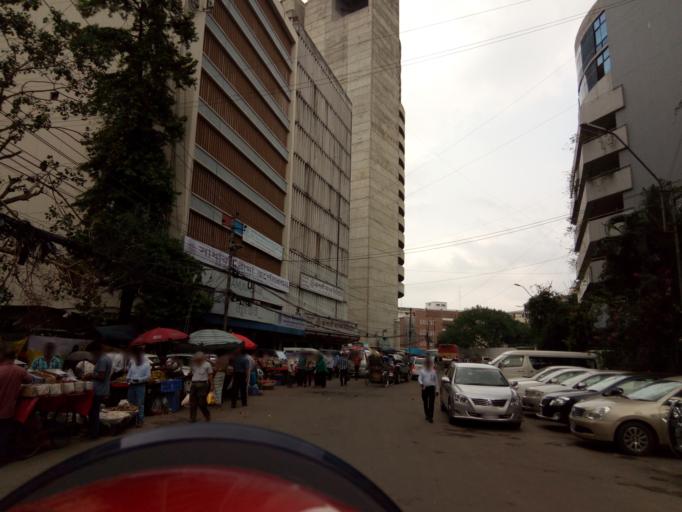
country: BD
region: Dhaka
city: Paltan
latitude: 23.7266
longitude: 90.4197
